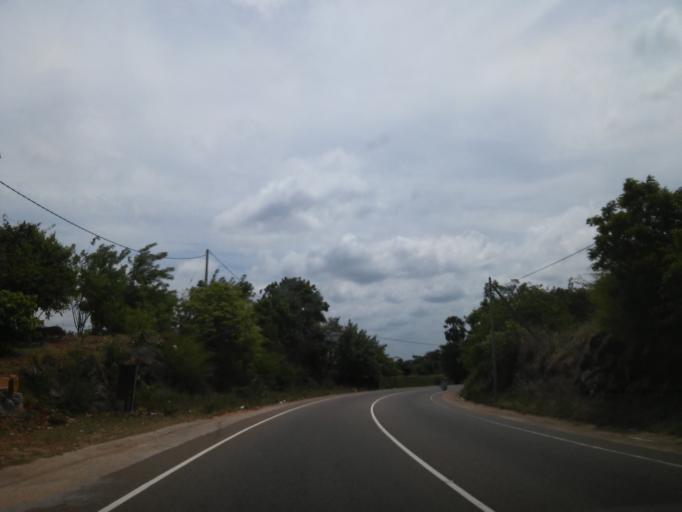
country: LK
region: Eastern Province
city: Trincomalee
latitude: 8.3359
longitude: 80.9769
